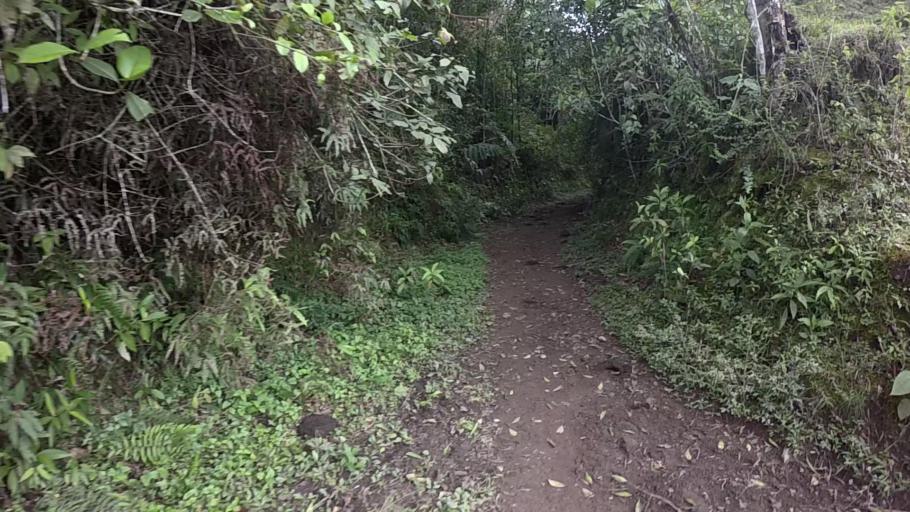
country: CO
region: Quindio
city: Salento
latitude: 4.6525
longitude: -75.5754
